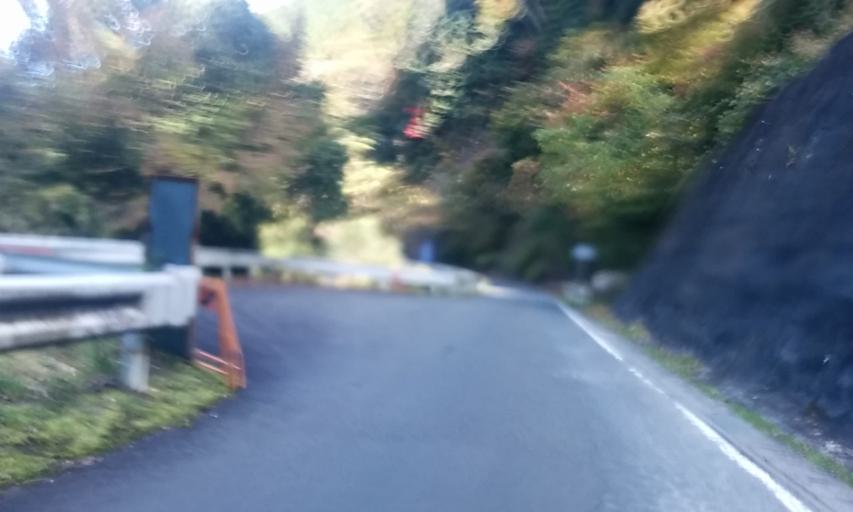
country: JP
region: Kyoto
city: Kameoka
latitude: 35.1320
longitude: 135.5751
